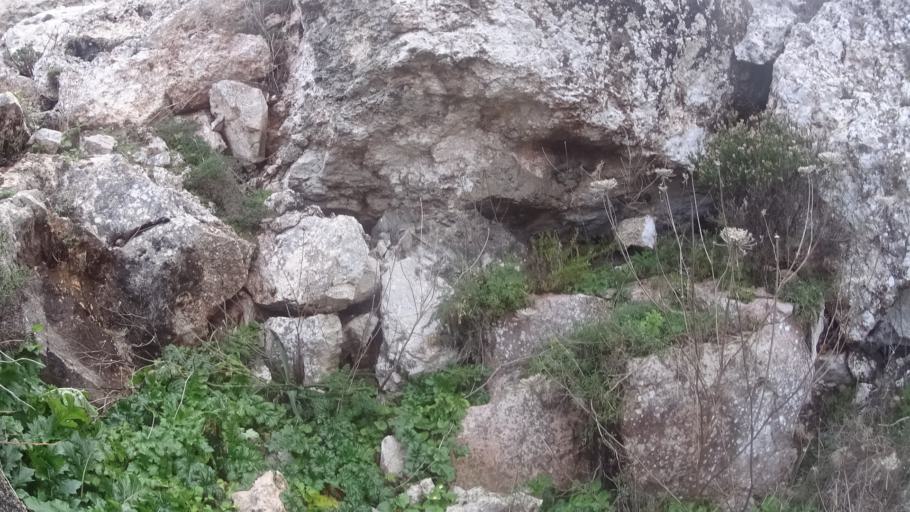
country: MT
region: Il-Mellieha
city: Mellieha
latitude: 35.9787
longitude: 14.3279
